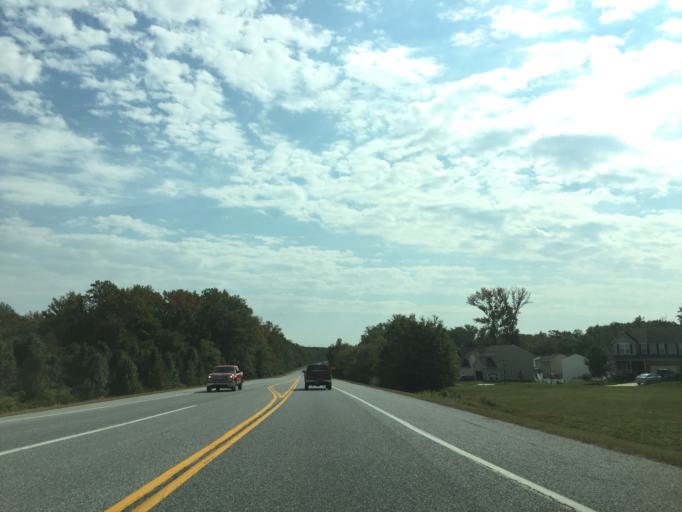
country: US
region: Maryland
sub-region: Harford County
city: Edgewood
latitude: 39.4171
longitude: -76.3074
